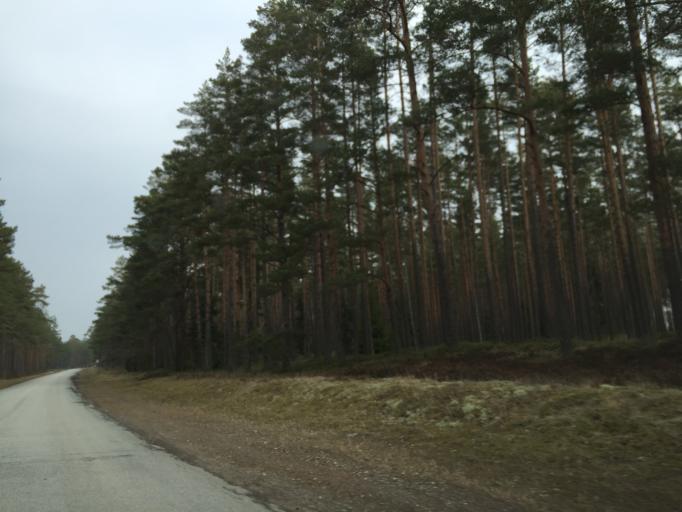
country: LV
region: Salacgrivas
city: Ainazi
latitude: 57.9696
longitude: 24.4088
